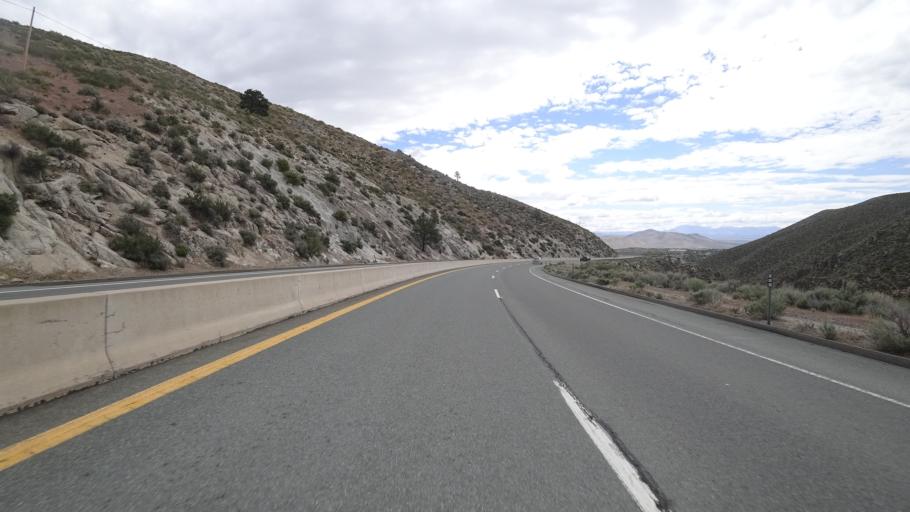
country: US
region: Nevada
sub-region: Douglas County
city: Indian Hills
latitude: 39.1165
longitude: -119.8013
